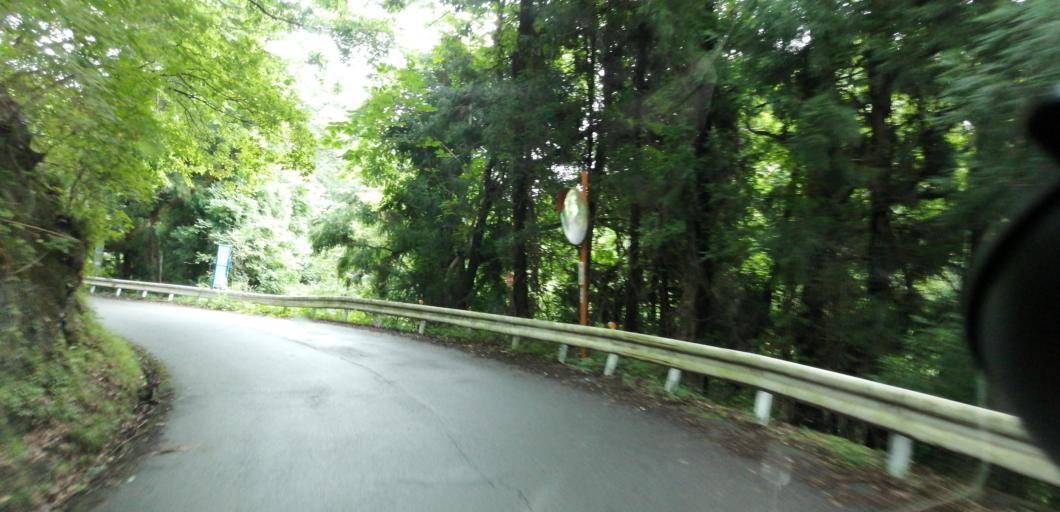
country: JP
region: Saitama
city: Chichibu
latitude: 36.0353
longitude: 139.1148
